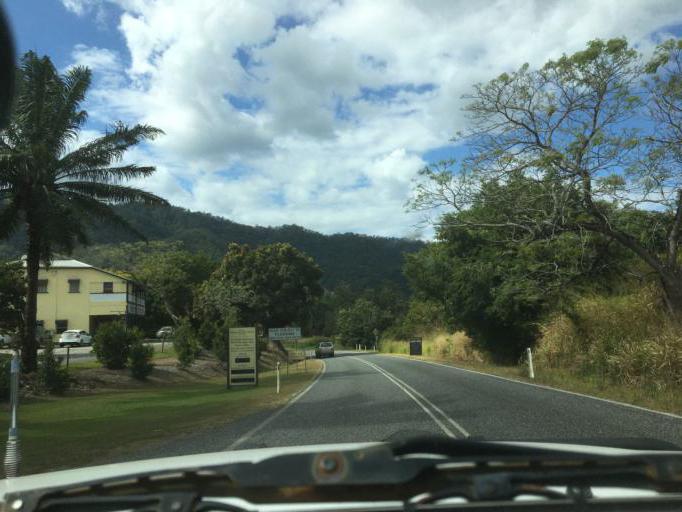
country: AU
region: Queensland
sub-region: Cairns
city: Woree
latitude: -17.1414
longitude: 145.7230
